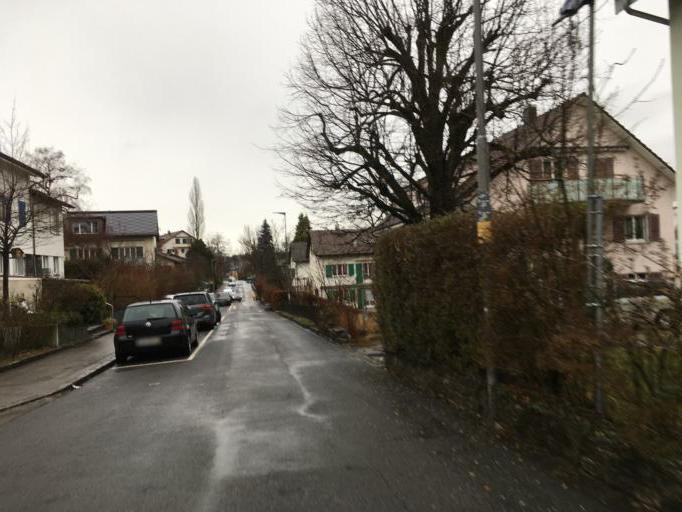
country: CH
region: Bern
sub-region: Bern-Mittelland District
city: Bolligen
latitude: 46.9573
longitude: 7.4791
